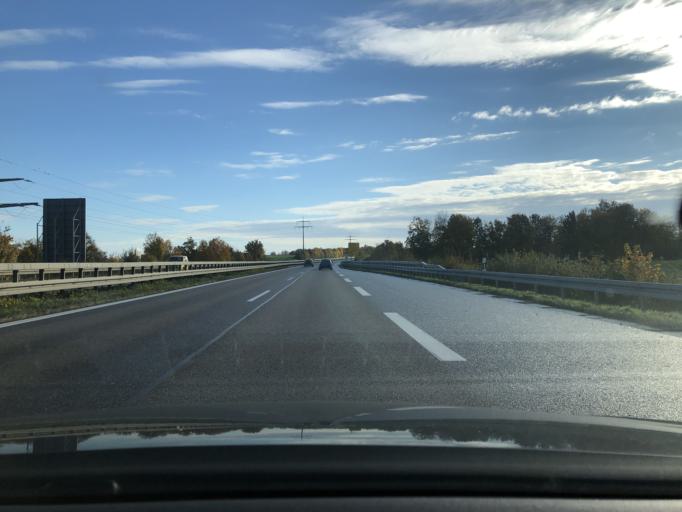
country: DE
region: Baden-Wuerttemberg
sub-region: Regierungsbezirk Stuttgart
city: Filderstadt
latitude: 48.6647
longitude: 9.2129
